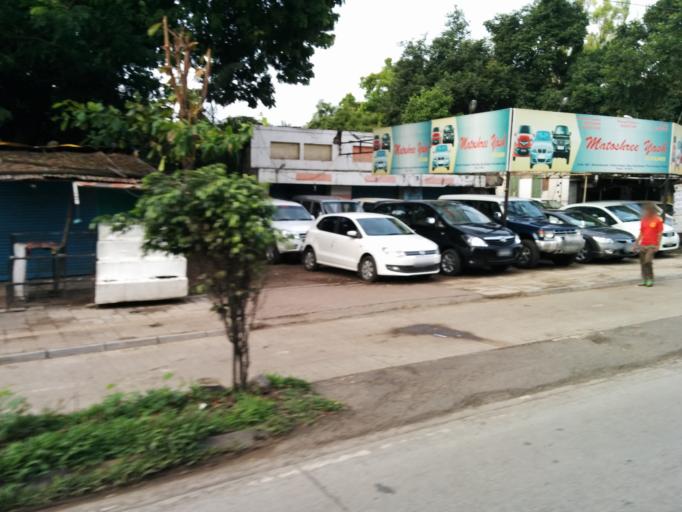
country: IN
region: Maharashtra
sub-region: Pune Division
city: Pune
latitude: 18.5064
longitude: 73.9037
